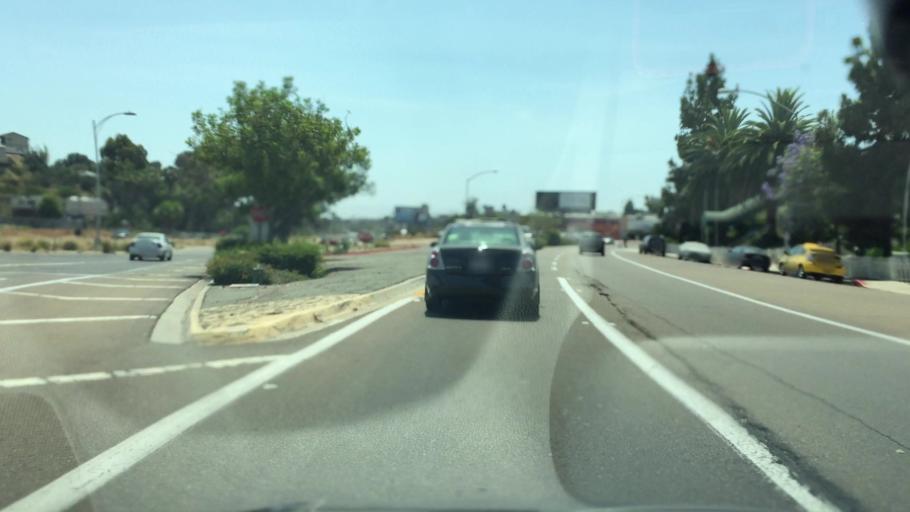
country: US
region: California
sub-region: San Diego County
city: Lemon Grove
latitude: 32.7483
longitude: -117.0737
